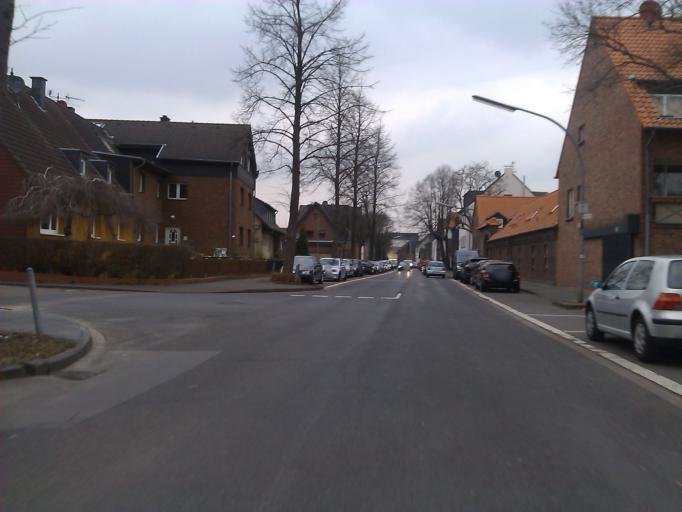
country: DE
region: North Rhine-Westphalia
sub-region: Regierungsbezirk Koln
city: Leverkusen
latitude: 51.0226
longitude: 6.9608
